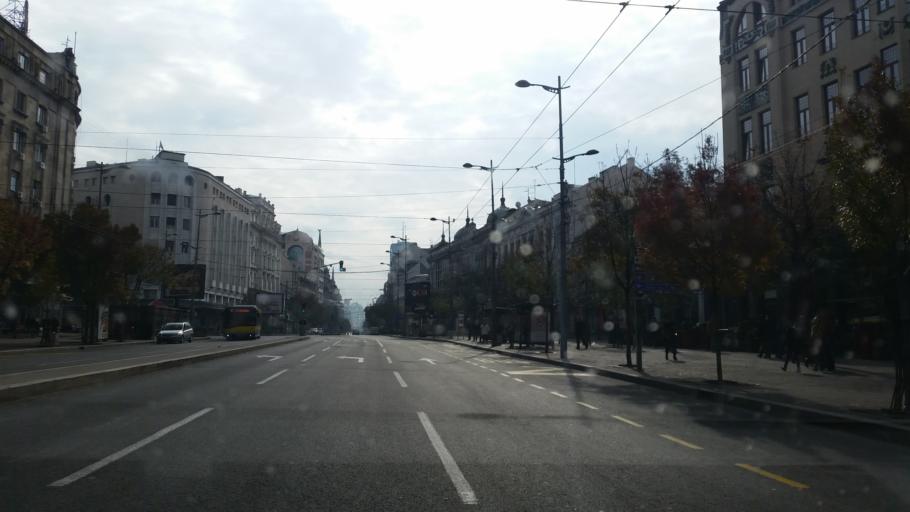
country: RS
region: Central Serbia
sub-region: Belgrade
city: Stari Grad
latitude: 44.8132
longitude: 20.4609
